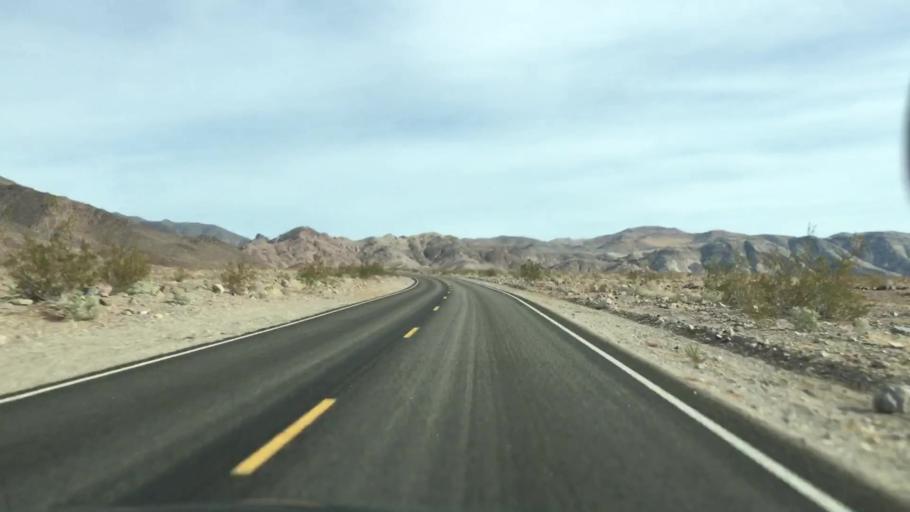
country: US
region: Nevada
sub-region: Nye County
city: Beatty
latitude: 36.7102
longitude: -116.9865
